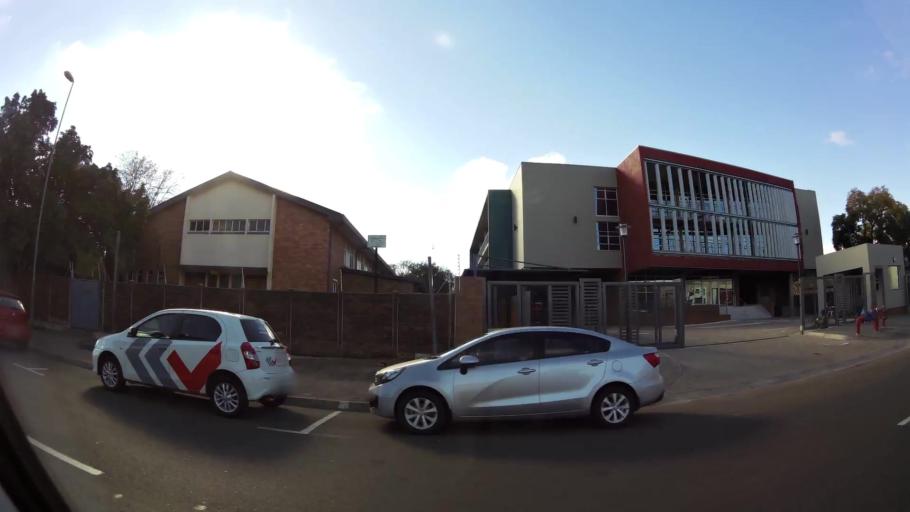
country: ZA
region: Limpopo
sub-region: Capricorn District Municipality
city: Polokwane
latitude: -23.9114
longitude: 29.4569
